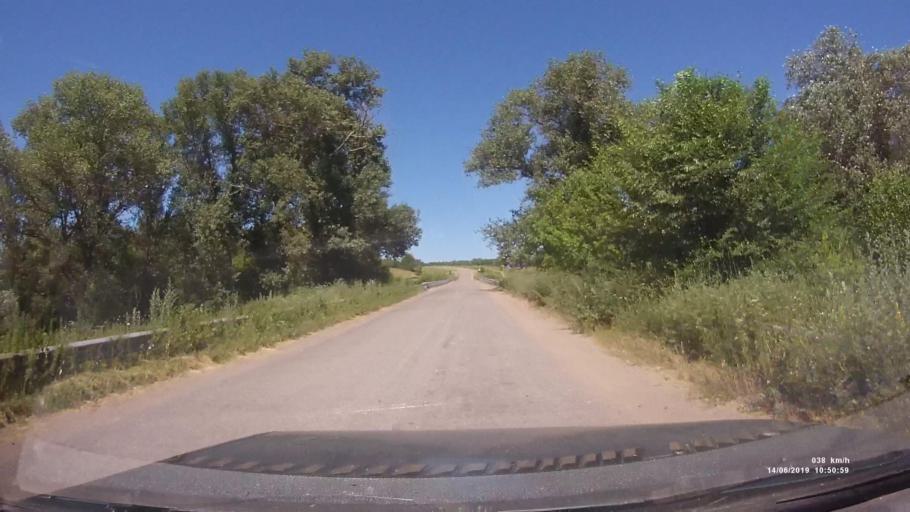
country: RU
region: Rostov
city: Kazanskaya
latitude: 49.8681
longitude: 41.3952
